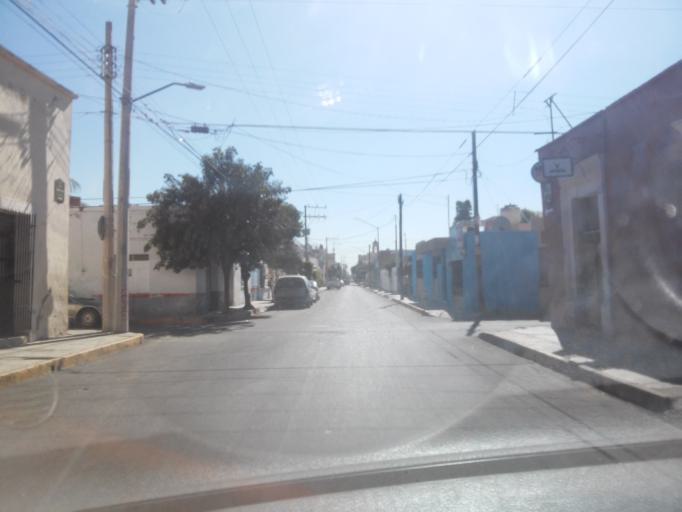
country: MX
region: Durango
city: Victoria de Durango
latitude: 24.0315
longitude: -104.6689
